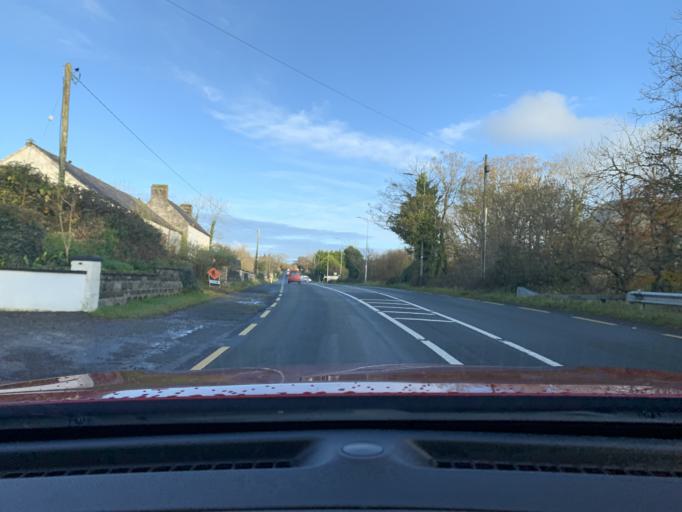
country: IE
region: Connaught
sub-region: Sligo
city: Sligo
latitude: 54.3401
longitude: -8.5026
